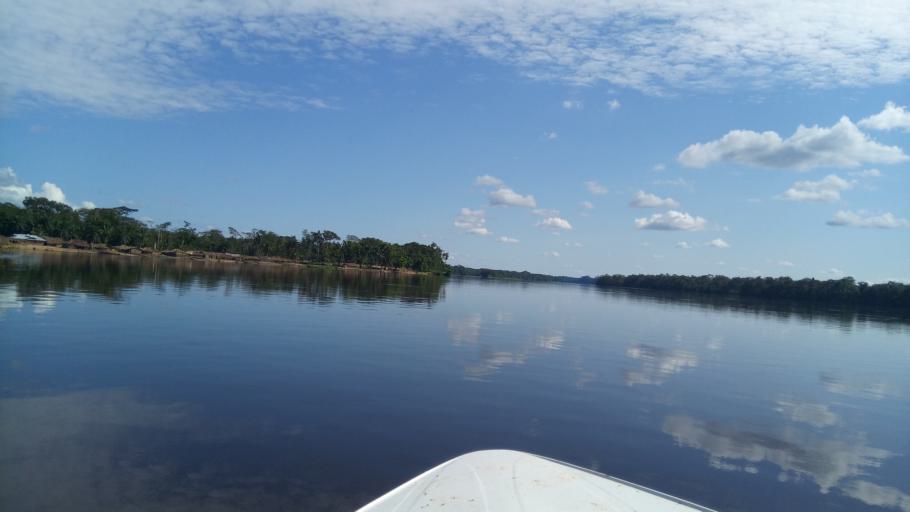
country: CD
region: Eastern Province
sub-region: Sous-Region de la Tshopo
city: Yangambi
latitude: 0.5295
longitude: 24.1947
